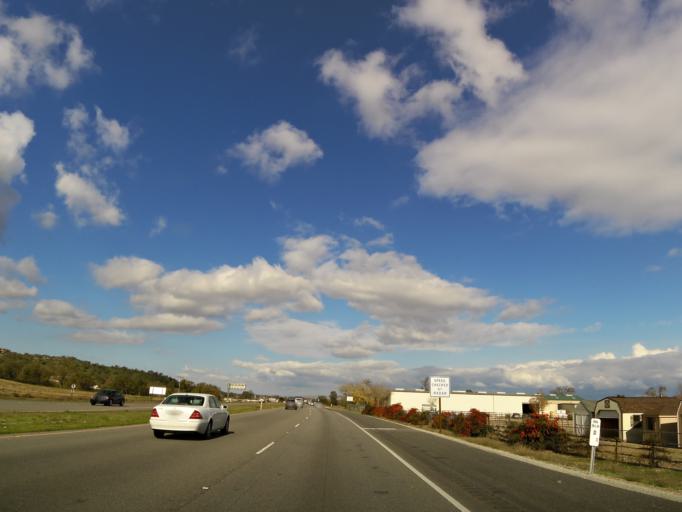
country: US
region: California
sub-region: San Luis Obispo County
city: Paso Robles
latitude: 35.6684
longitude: -120.6959
